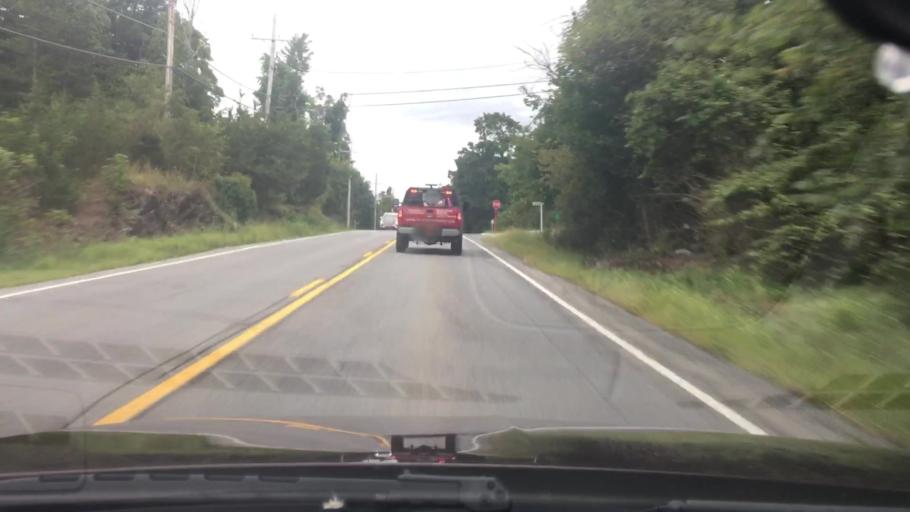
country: US
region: New York
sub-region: Dutchess County
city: Pleasant Valley
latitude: 41.7651
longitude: -73.7785
